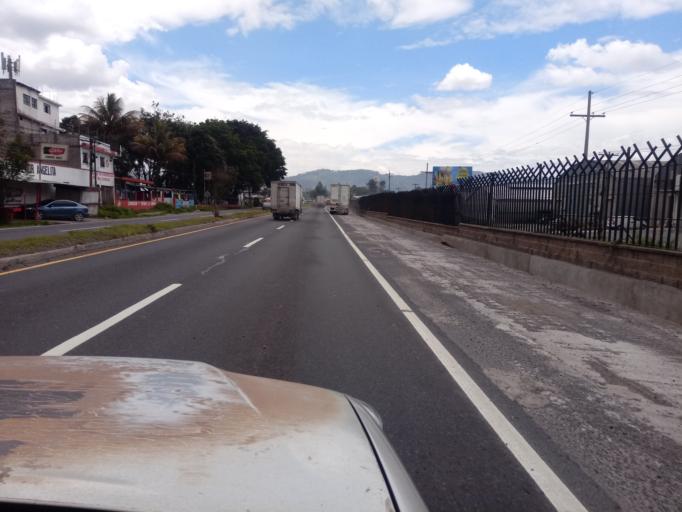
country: GT
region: Guatemala
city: Amatitlan
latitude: 14.4607
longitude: -90.6428
